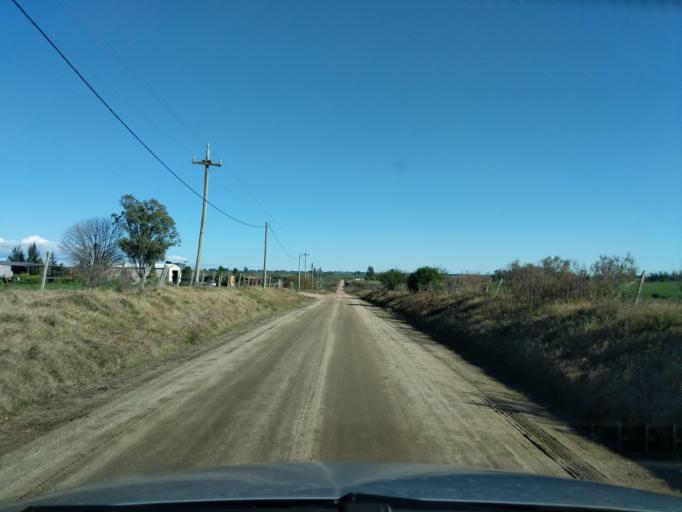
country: UY
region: Florida
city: Florida
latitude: -34.0815
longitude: -56.2548
